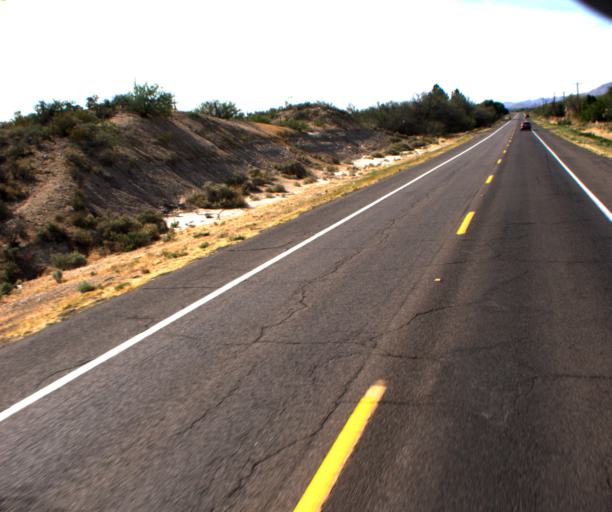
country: US
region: Arizona
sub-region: Graham County
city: Swift Trail Junction
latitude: 32.7015
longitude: -109.7078
